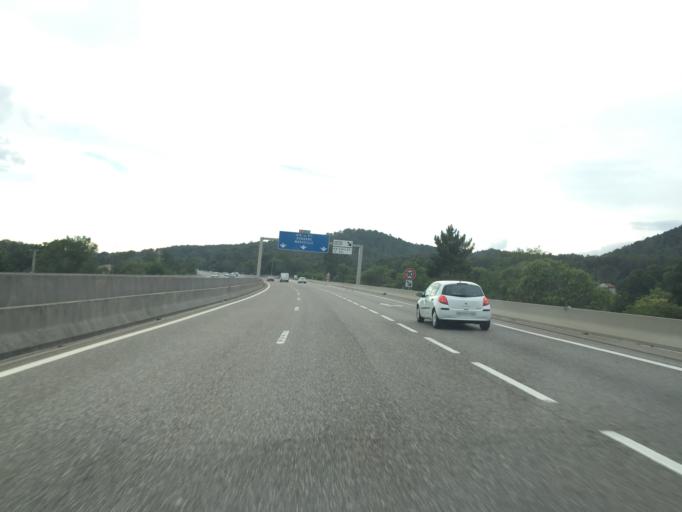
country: FR
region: Provence-Alpes-Cote d'Azur
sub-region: Departement du Var
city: Le Val
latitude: 43.4217
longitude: 6.0742
